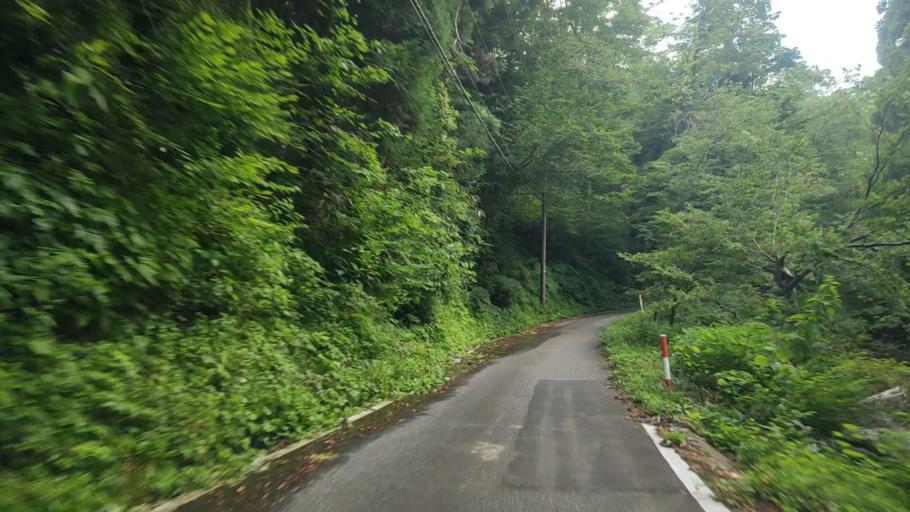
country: JP
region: Fukui
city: Katsuyama
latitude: 36.1999
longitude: 136.5254
